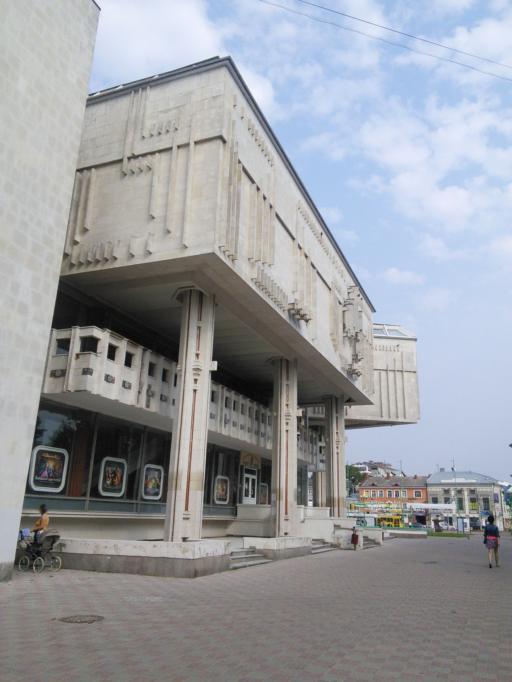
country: RU
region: Jaroslavl
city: Yaroslavl
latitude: 57.6242
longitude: 39.8771
